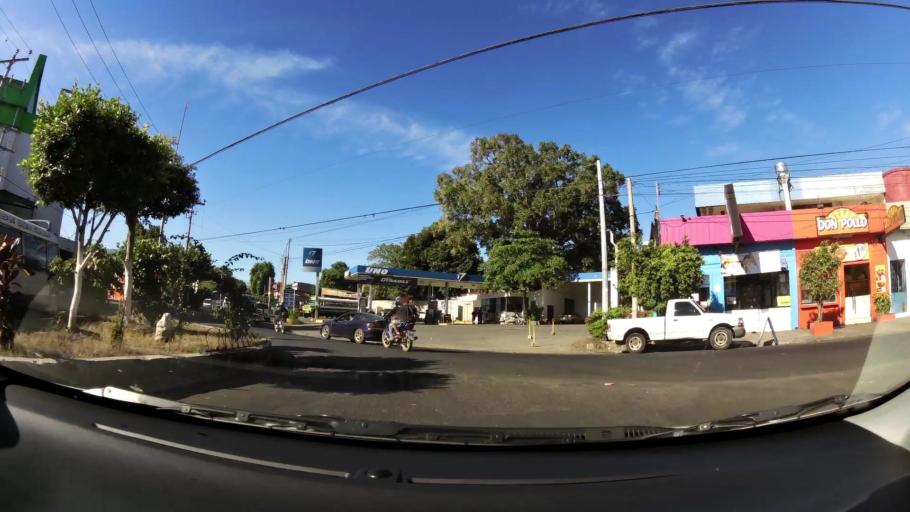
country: SV
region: Santa Ana
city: Santa Ana
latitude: 13.9891
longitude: -89.5650
